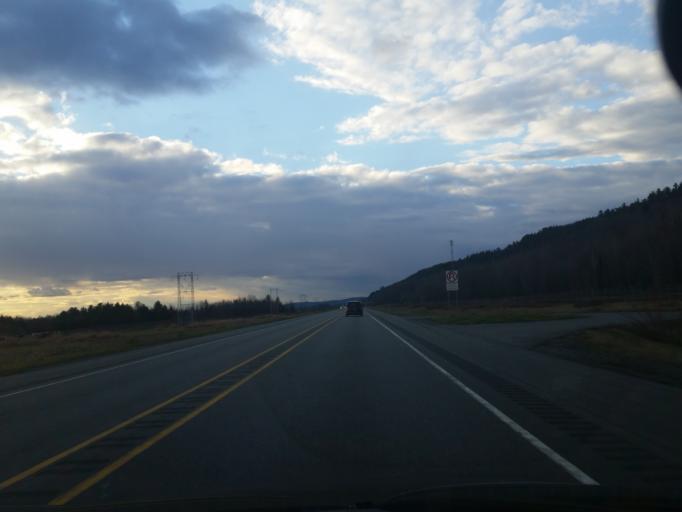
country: CA
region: Ontario
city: Hawkesbury
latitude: 45.6520
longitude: -74.7830
